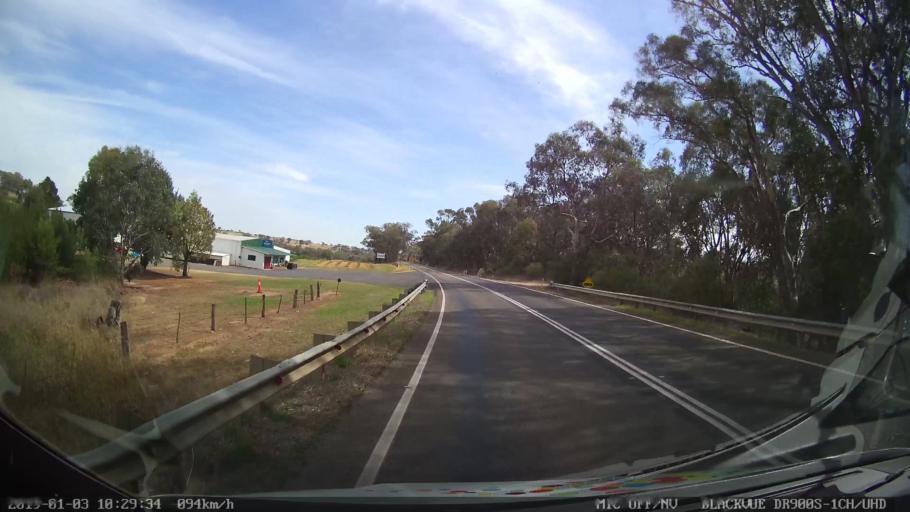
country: AU
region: New South Wales
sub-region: Young
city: Young
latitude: -34.3726
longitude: 148.2615
